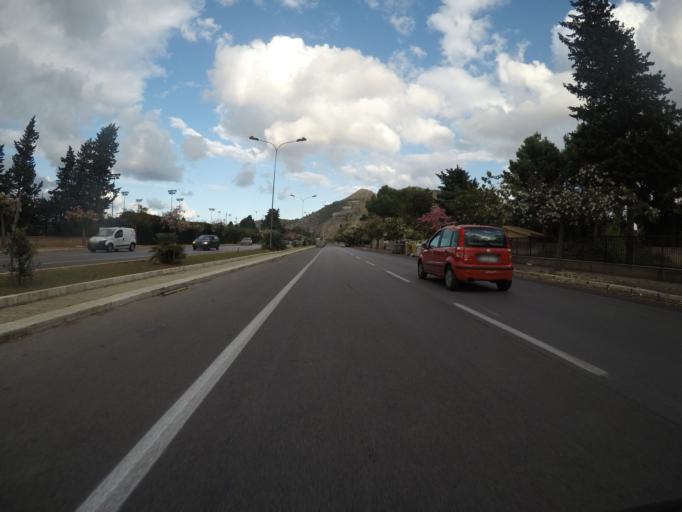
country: IT
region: Sicily
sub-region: Palermo
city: Palermo
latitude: 38.1889
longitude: 13.3179
